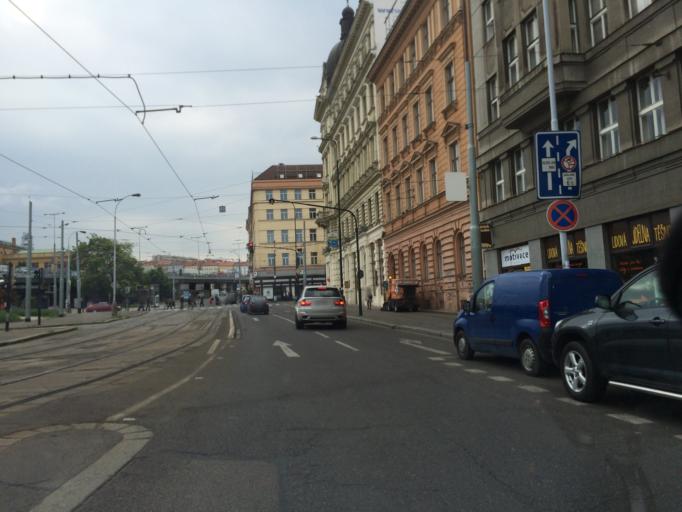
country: CZ
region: Praha
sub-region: Praha 8
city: Karlin
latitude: 50.0913
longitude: 14.4364
